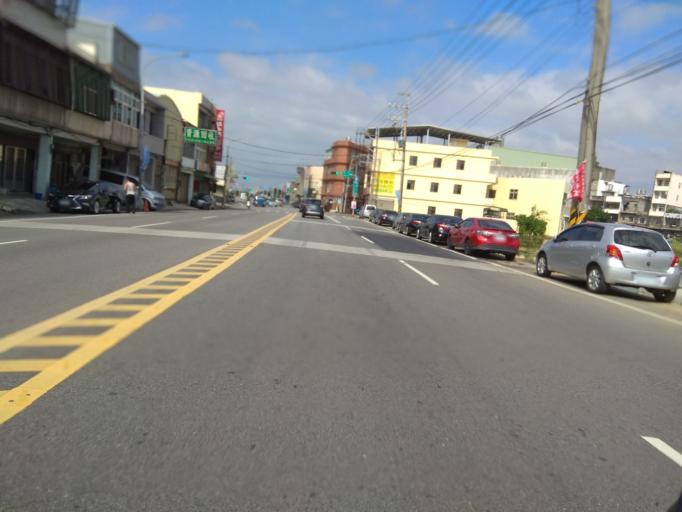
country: TW
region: Taiwan
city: Taoyuan City
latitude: 25.0515
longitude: 121.2243
